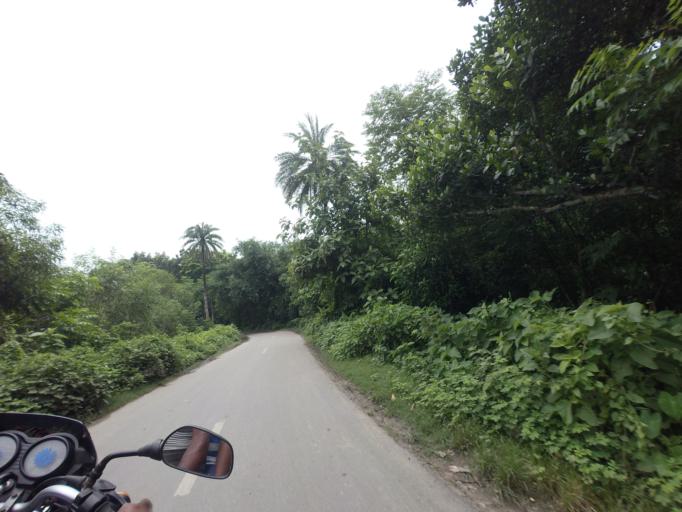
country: BD
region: Khulna
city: Kalia
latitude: 23.1164
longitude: 89.6473
